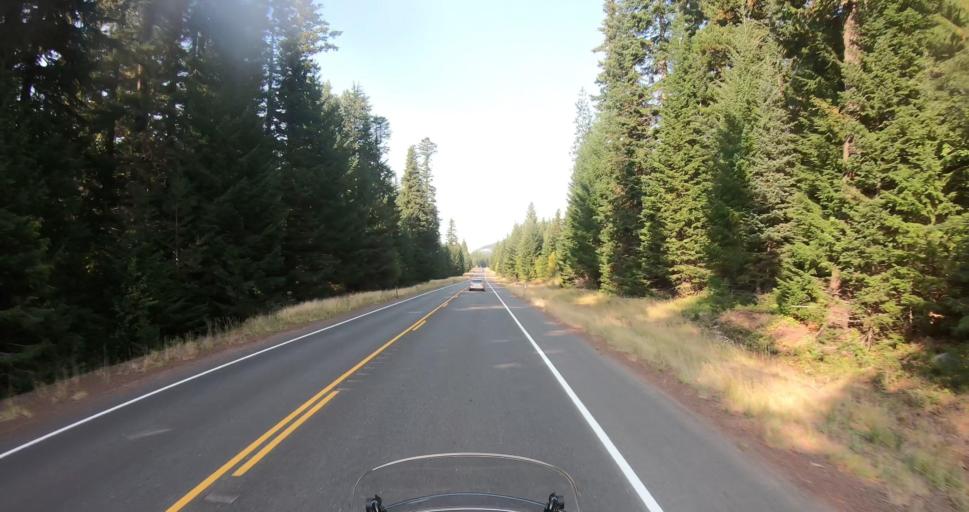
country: US
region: Oregon
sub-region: Hood River County
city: Odell
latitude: 45.3588
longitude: -121.5681
